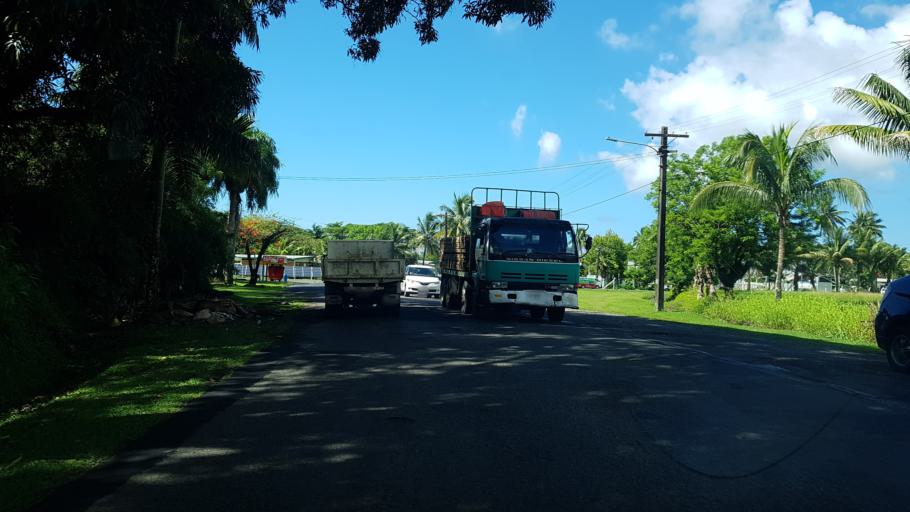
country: FJ
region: Central
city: Suva
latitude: -18.1479
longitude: 178.4529
